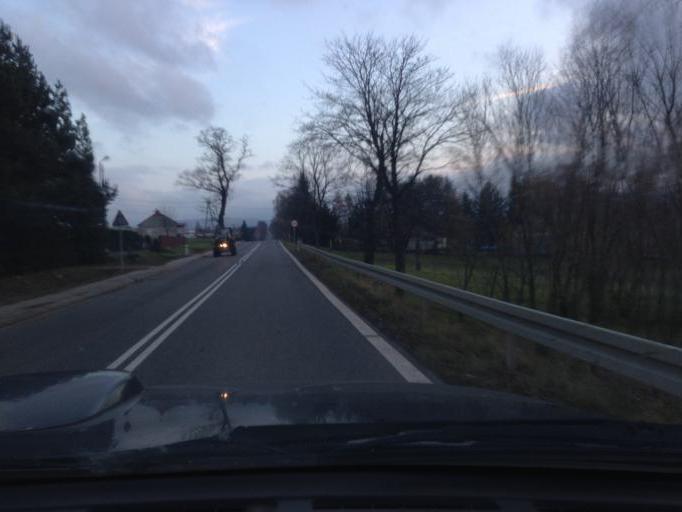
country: PL
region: Subcarpathian Voivodeship
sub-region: Powiat jasielski
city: Nowy Zmigrod
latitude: 49.6362
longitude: 21.5249
